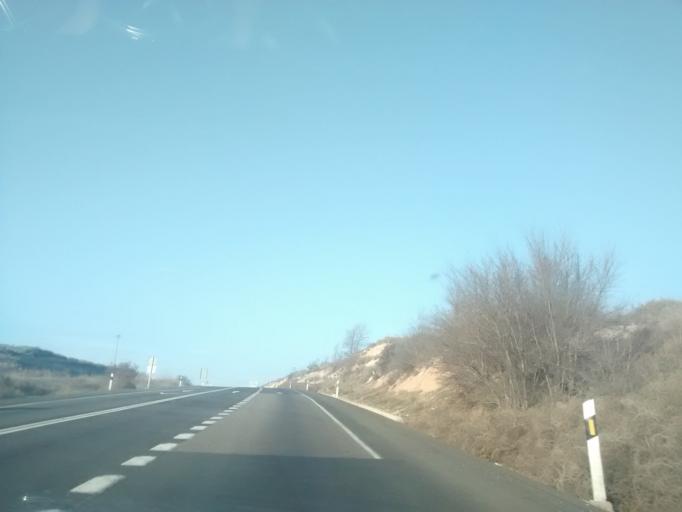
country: ES
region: Aragon
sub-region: Provincia de Huesca
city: Fraga
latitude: 41.5136
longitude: 0.2745
